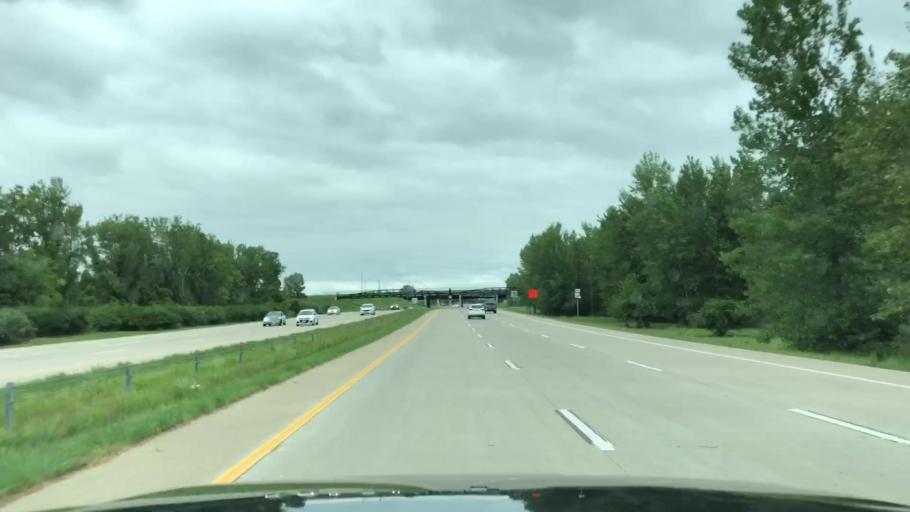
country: US
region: Missouri
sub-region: Saint Louis County
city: Maryland Heights
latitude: 38.7028
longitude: -90.5028
